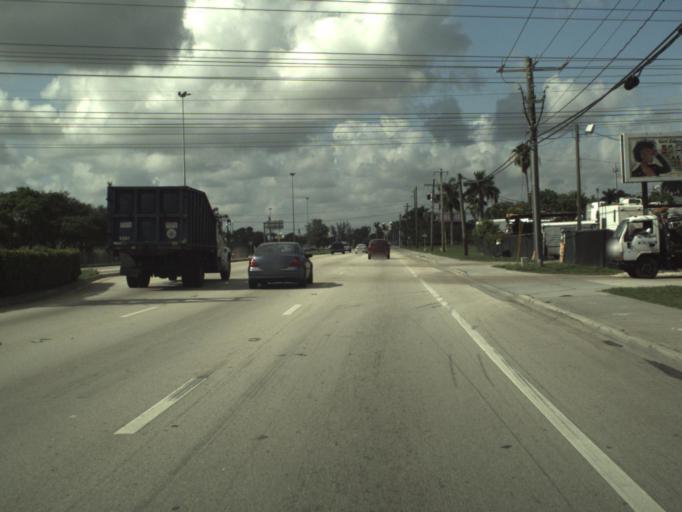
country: US
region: Florida
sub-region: Broward County
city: Broadview Park
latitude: 26.0730
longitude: -80.2066
